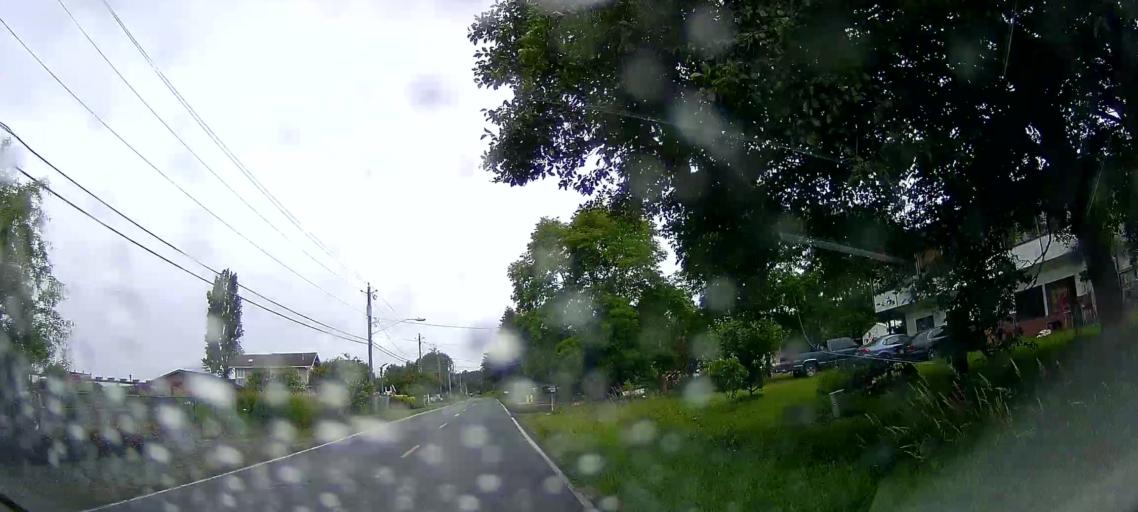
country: US
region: Washington
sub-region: Whatcom County
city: Birch Bay
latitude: 48.8082
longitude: -122.7086
